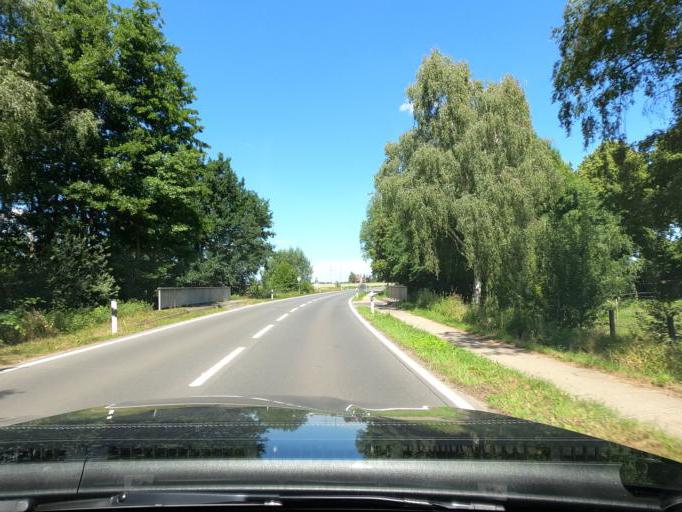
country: DE
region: Lower Saxony
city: Lehrte
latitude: 52.4049
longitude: 9.9737
